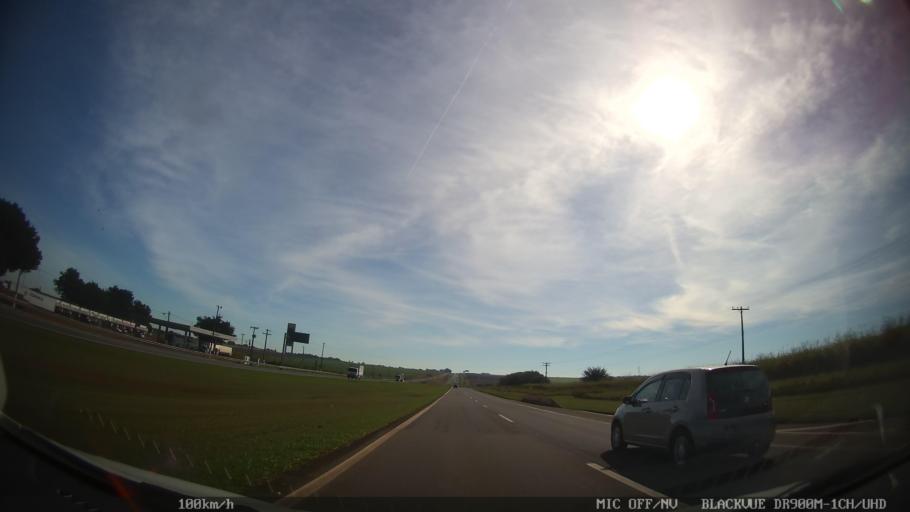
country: BR
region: Sao Paulo
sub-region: Cordeiropolis
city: Cordeiropolis
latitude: -22.4872
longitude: -47.3991
